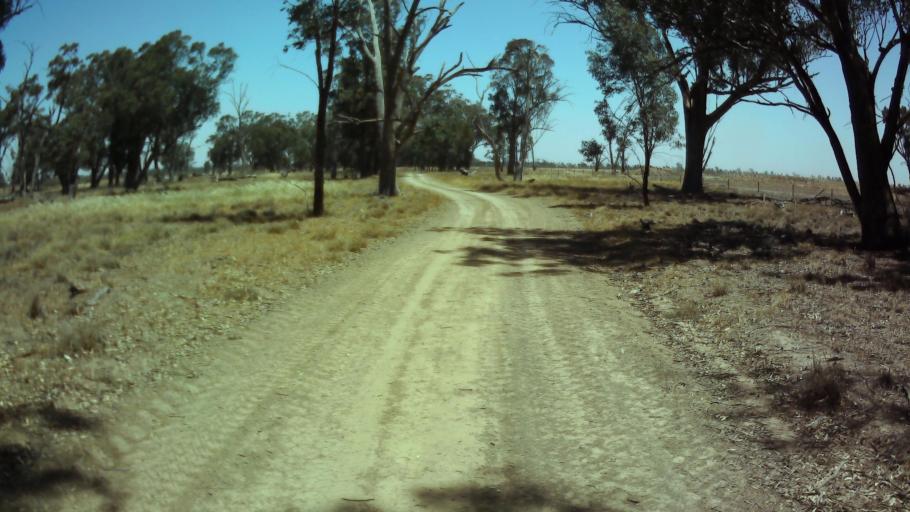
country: AU
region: New South Wales
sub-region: Weddin
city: Grenfell
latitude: -34.0517
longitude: 147.8275
